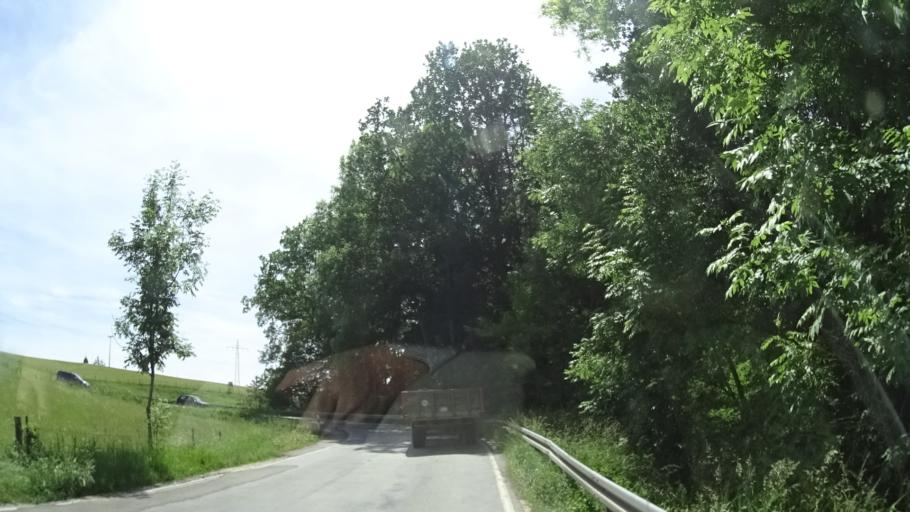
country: DE
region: Baden-Wuerttemberg
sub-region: Regierungsbezirk Stuttgart
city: Abtsgmund
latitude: 48.9203
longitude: 9.9968
